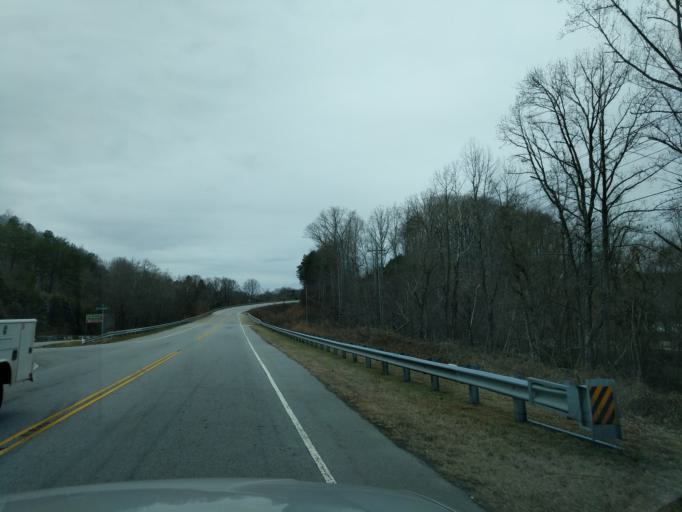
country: US
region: South Carolina
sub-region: Greenville County
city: Slater-Marietta
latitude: 35.0847
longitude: -82.4583
